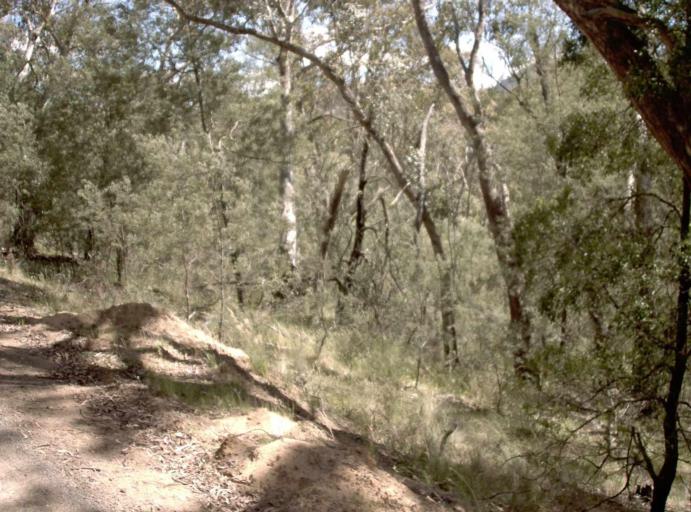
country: AU
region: New South Wales
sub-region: Bombala
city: Bombala
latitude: -37.1363
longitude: 148.6612
